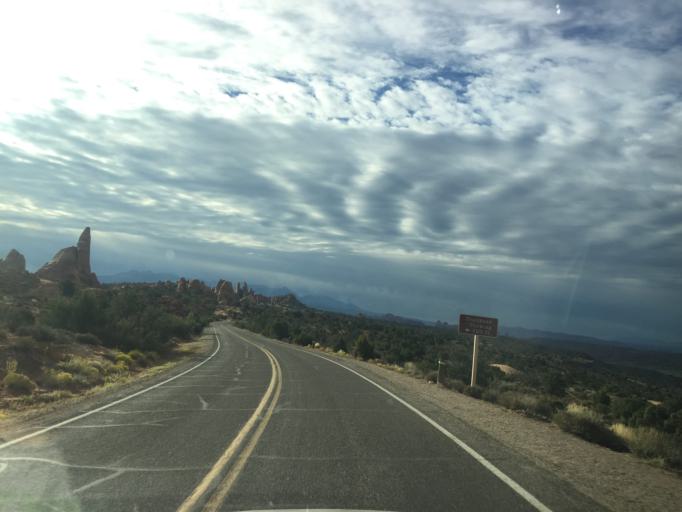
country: US
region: Utah
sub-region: Grand County
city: Moab
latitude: 38.7729
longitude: -109.5921
